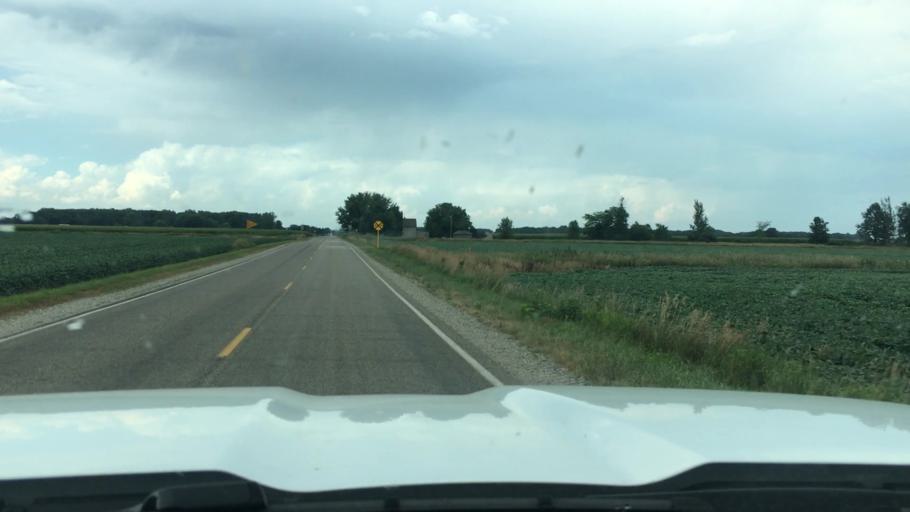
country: US
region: Michigan
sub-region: Montcalm County
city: Carson City
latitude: 43.1814
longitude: -84.7781
